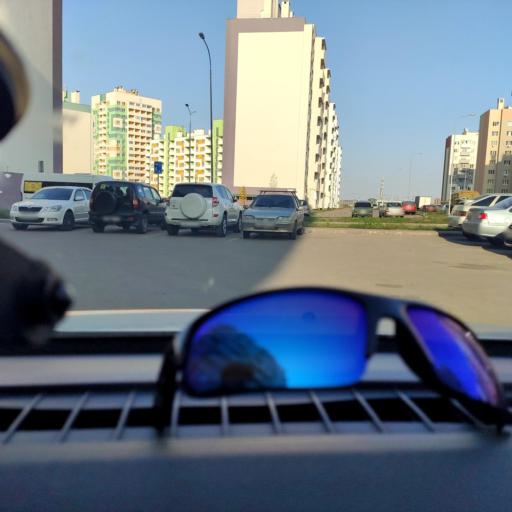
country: RU
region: Samara
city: Samara
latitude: 53.0945
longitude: 50.1642
